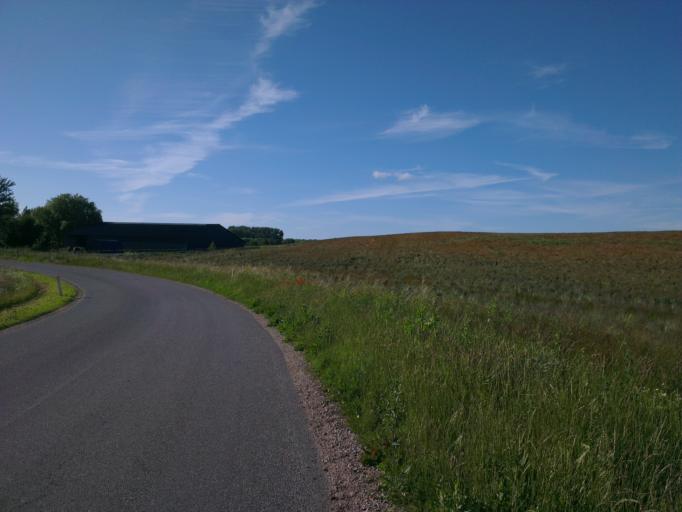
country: DK
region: Capital Region
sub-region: Frederikssund Kommune
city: Skibby
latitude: 55.7595
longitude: 12.0357
